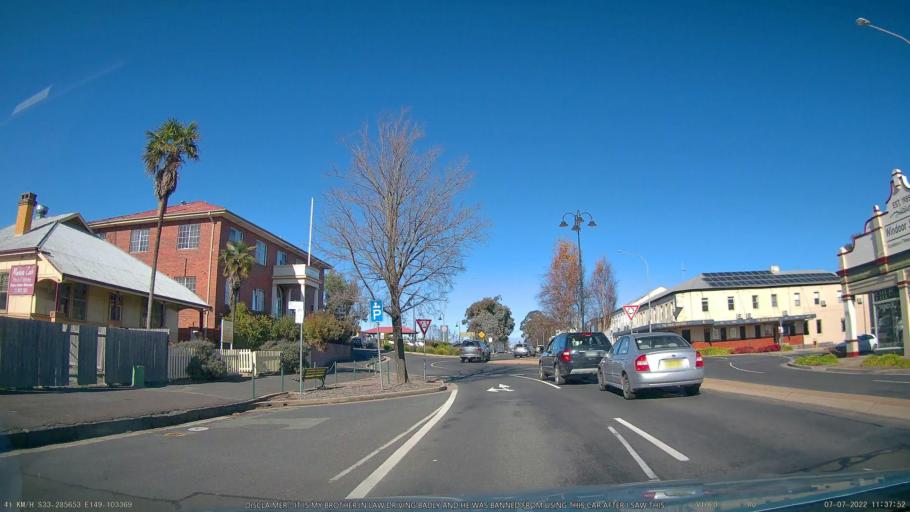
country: AU
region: New South Wales
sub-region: Orange Municipality
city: Orange
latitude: -33.2859
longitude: 149.1033
